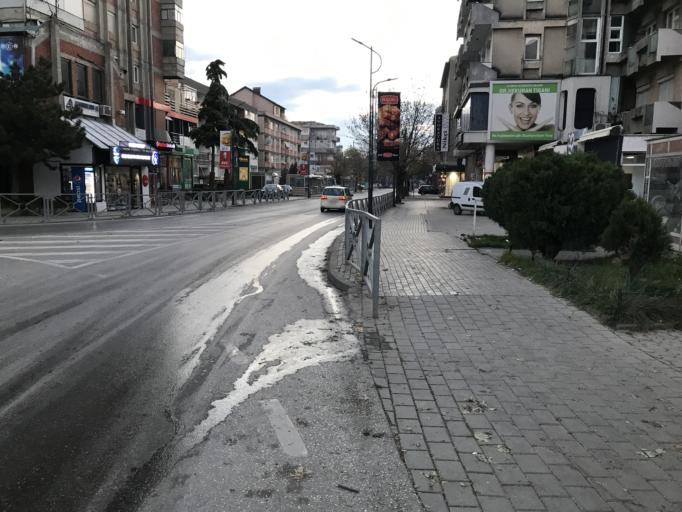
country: XK
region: Pec
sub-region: Komuna e Pejes
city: Peje
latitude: 42.6622
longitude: 20.2967
